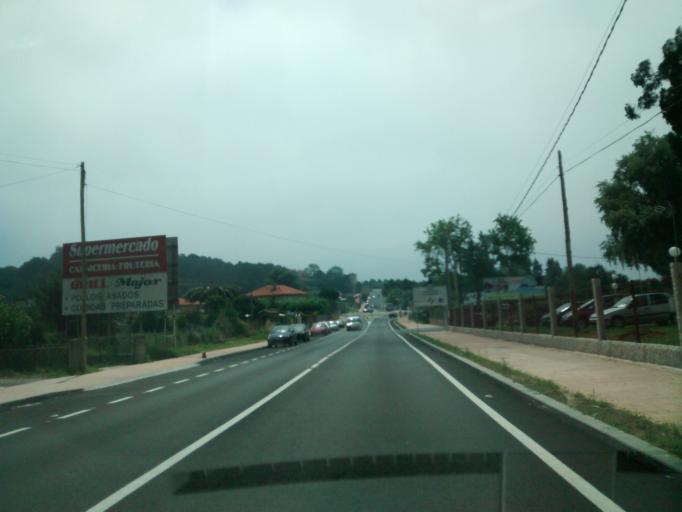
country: ES
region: Galicia
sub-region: Provincia de Pontevedra
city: Sanxenxo
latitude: 42.4181
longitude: -8.8697
